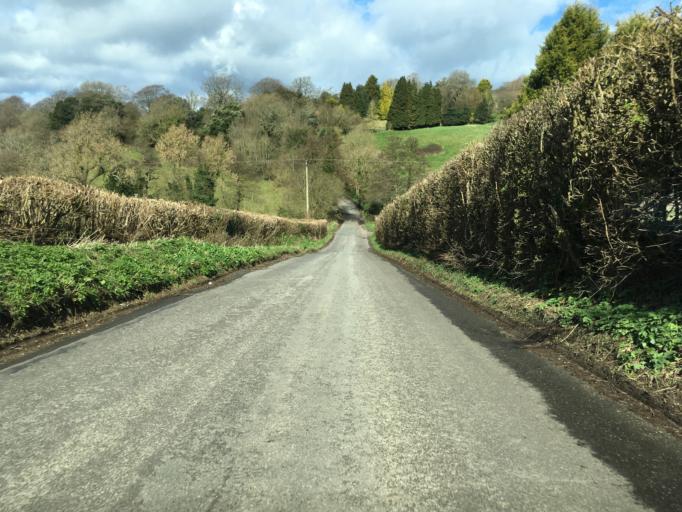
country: GB
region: England
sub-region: Gloucestershire
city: Wotton-under-Edge
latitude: 51.6124
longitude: -2.3343
